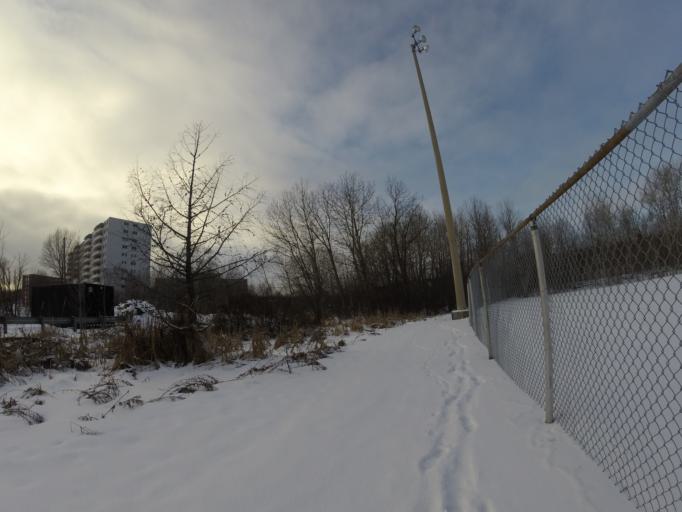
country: CA
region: Ontario
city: Greater Sudbury
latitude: 46.4694
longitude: -81.0021
